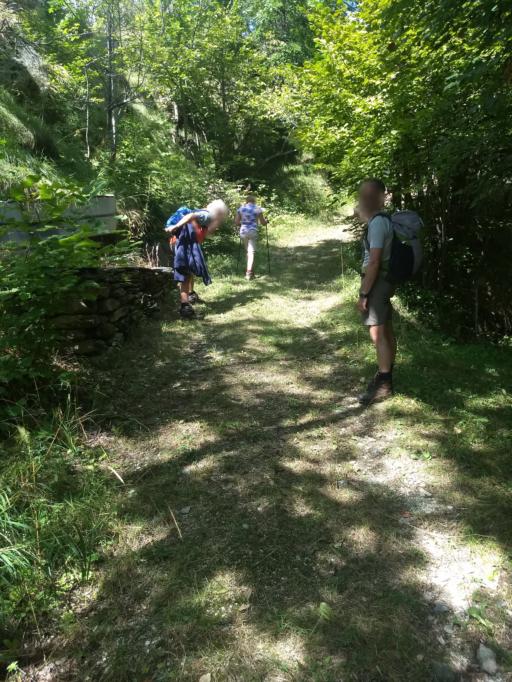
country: IT
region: Piedmont
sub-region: Provincia di Cuneo
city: Stroppo
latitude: 44.5128
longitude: 7.1189
